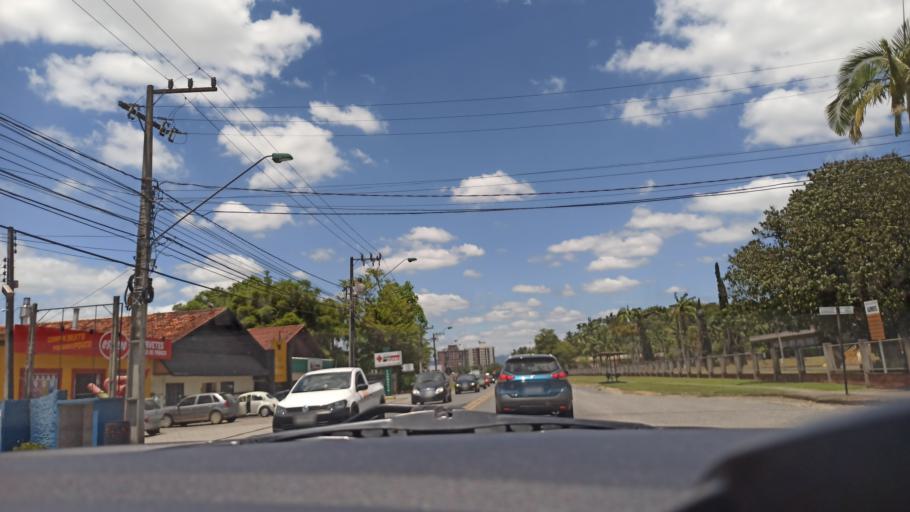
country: BR
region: Santa Catarina
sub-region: Blumenau
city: Blumenau
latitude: -26.8238
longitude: -49.0893
